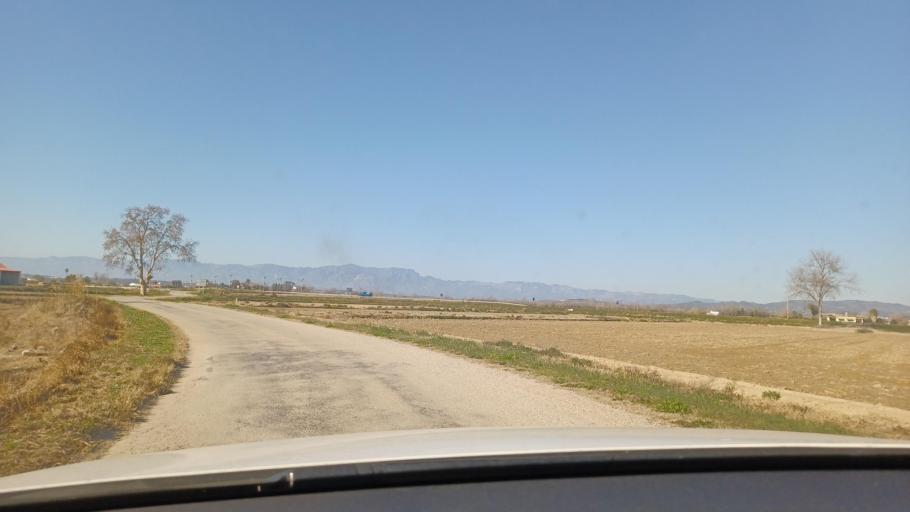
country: ES
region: Catalonia
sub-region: Provincia de Tarragona
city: Amposta
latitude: 40.7039
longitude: 0.6352
